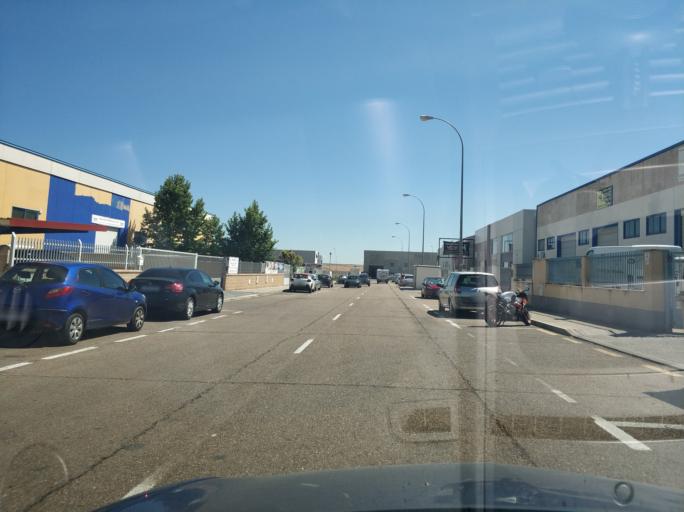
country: ES
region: Castille and Leon
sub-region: Provincia de Salamanca
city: Carbajosa de la Sagrada
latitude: 40.9381
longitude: -5.6552
